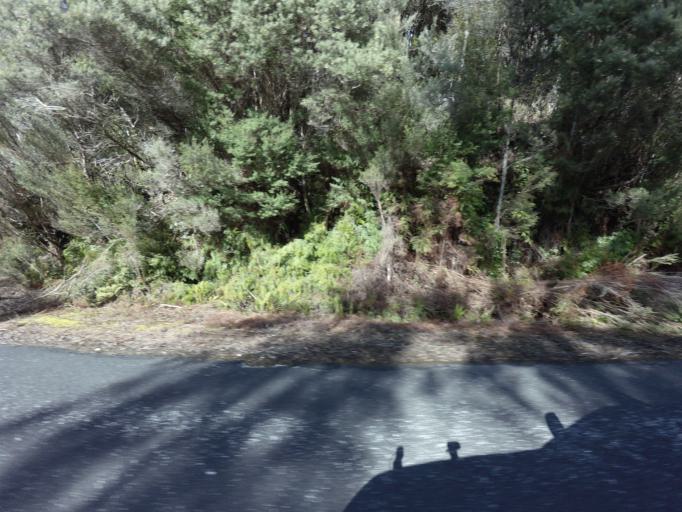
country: AU
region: Tasmania
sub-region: Huon Valley
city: Geeveston
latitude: -42.8134
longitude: 146.1012
